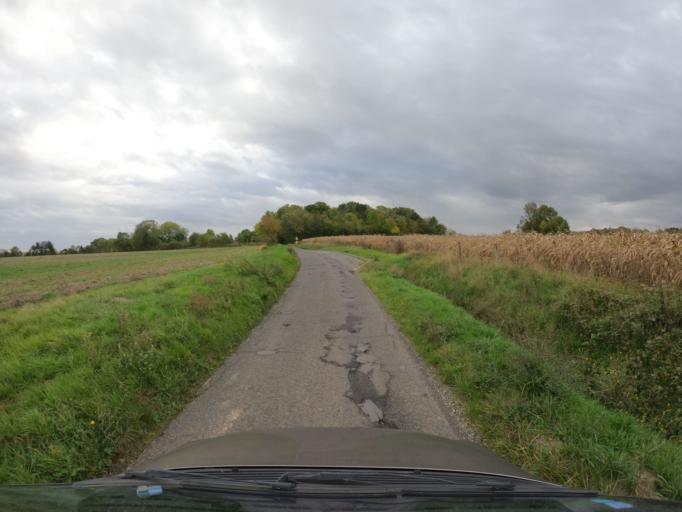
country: FR
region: Ile-de-France
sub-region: Departement de Seine-et-Marne
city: Montry
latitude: 48.8738
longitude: 2.8290
